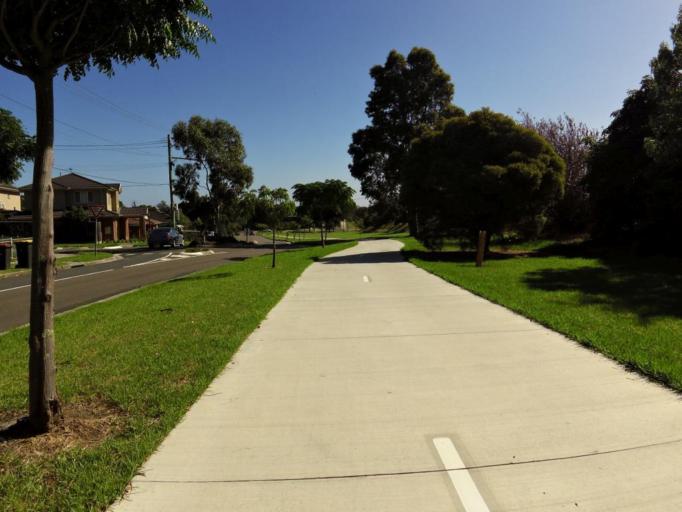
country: AU
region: Victoria
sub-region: Monash
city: Ashwood
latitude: -37.8736
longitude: 145.1026
